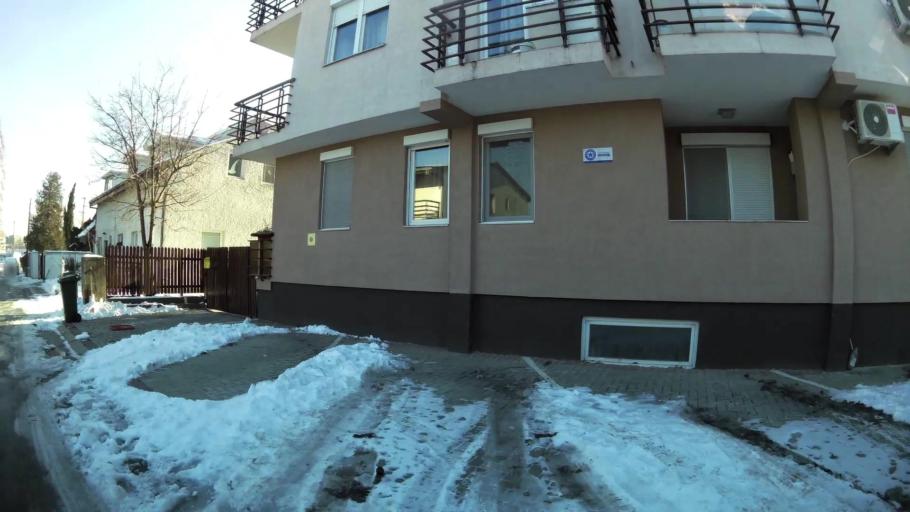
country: MK
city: Krushopek
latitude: 42.0039
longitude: 21.3766
